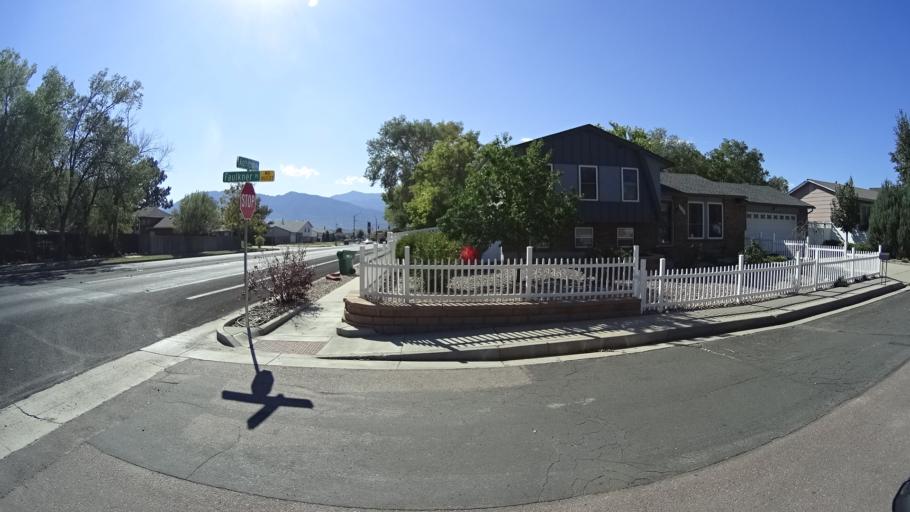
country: US
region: Colorado
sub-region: El Paso County
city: Stratmoor
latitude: 38.7967
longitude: -104.7540
